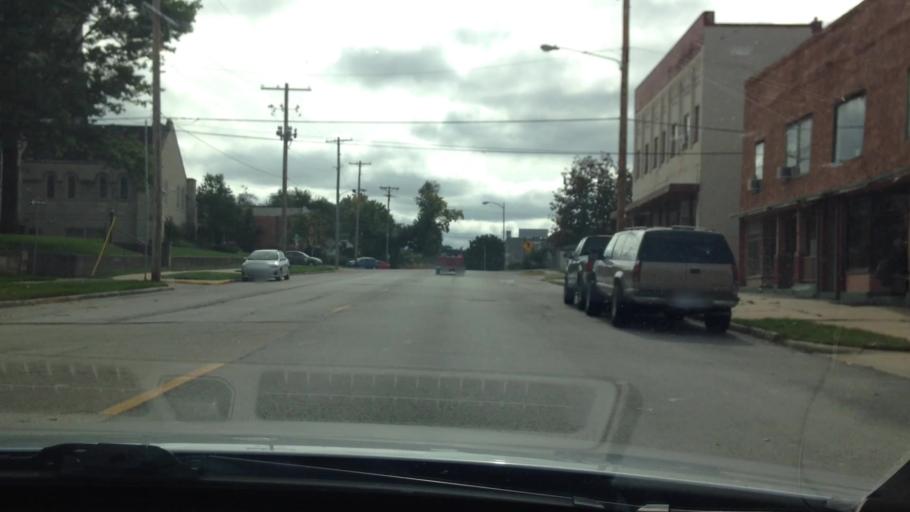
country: US
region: Kansas
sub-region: Leavenworth County
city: Leavenworth
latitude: 39.3136
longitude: -94.9144
